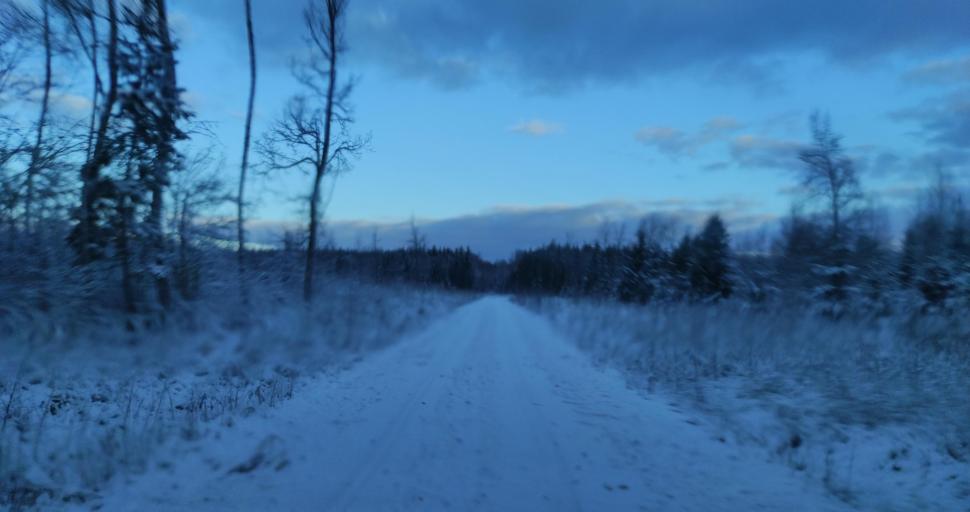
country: LV
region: Skrunda
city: Skrunda
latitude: 56.5805
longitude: 21.9193
